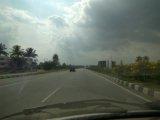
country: IN
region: Karnataka
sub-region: Kolar
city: Kolar
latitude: 13.1291
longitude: 77.9923
